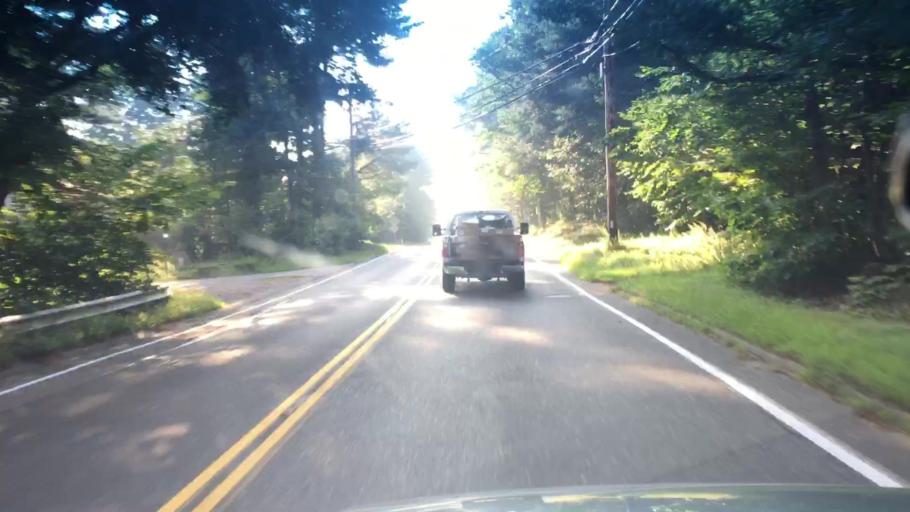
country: US
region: Massachusetts
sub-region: Norfolk County
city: Medfield
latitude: 42.1674
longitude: -71.2898
